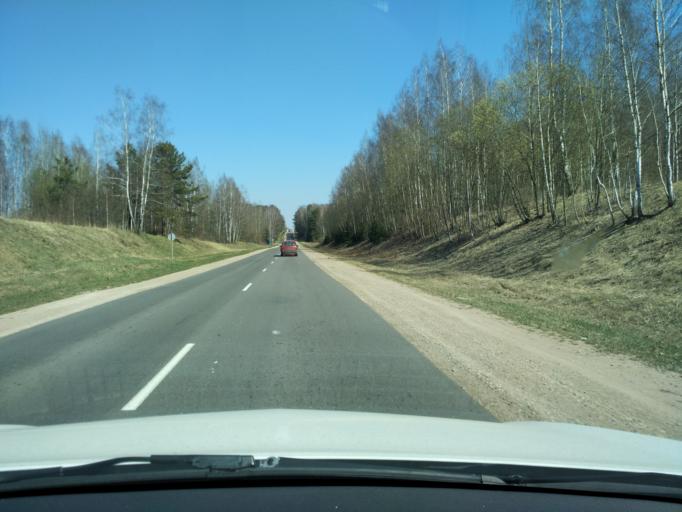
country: BY
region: Minsk
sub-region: Smalyavitski Rayon
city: Usjazh
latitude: 53.9970
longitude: 27.9867
